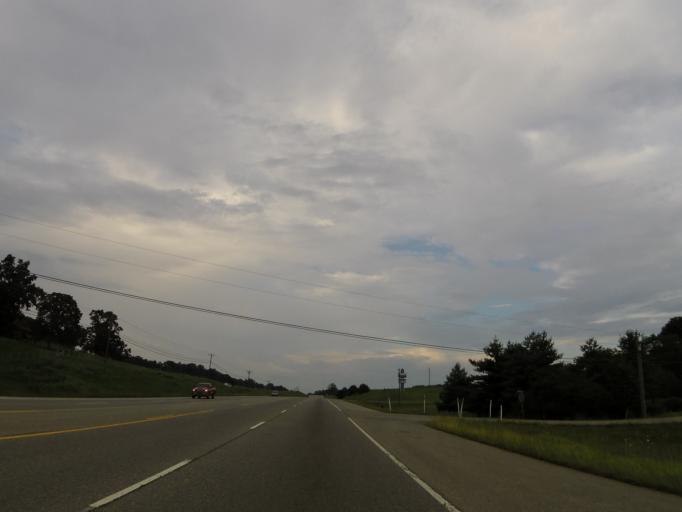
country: US
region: Tennessee
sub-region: Loudon County
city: Greenback
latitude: 35.6820
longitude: -84.0684
